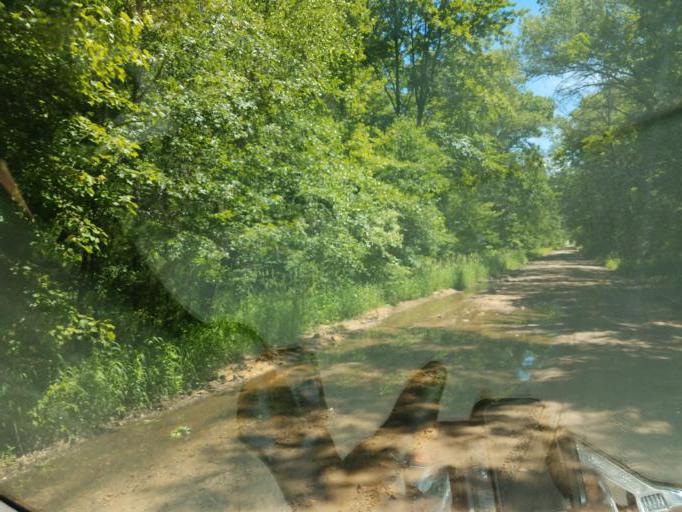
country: US
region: Wisconsin
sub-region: Adams County
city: Friendship
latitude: 44.0251
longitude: -89.9779
